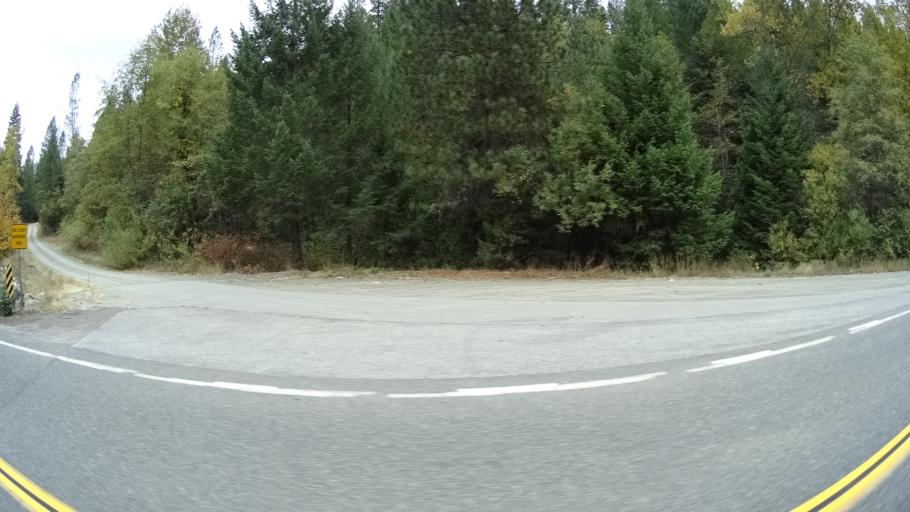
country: US
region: California
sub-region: Siskiyou County
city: Happy Camp
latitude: 41.9163
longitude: -123.4663
